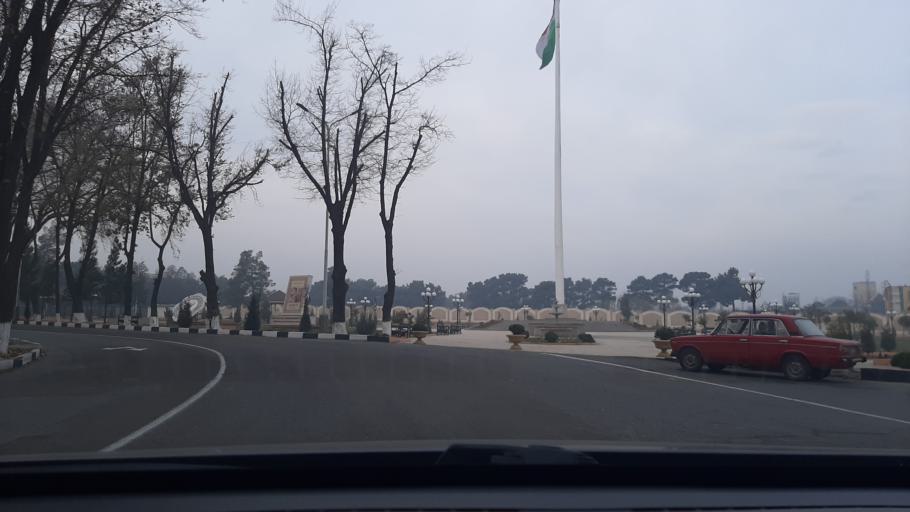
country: TJ
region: Viloyati Sughd
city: Chkalov
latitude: 40.2391
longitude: 69.6903
